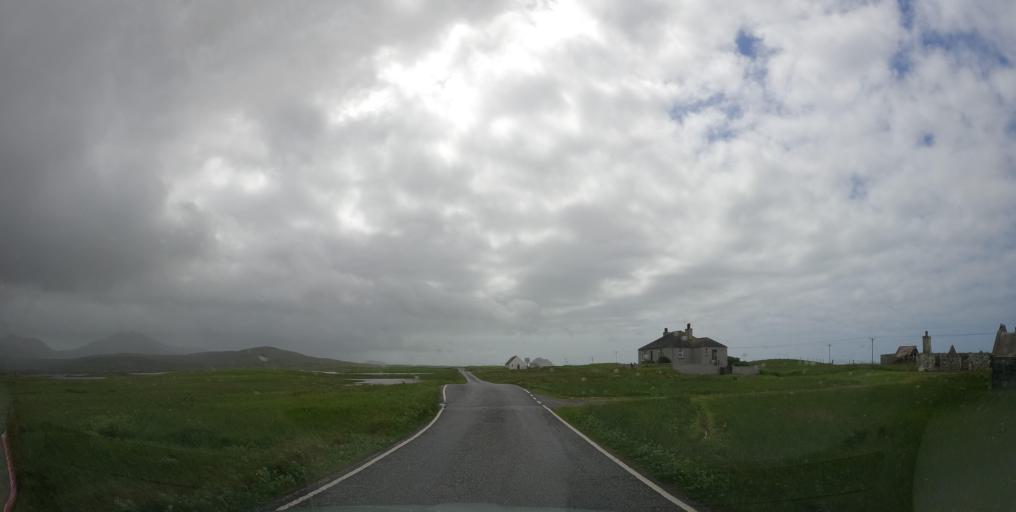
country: GB
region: Scotland
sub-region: Eilean Siar
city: Isle of South Uist
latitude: 57.3231
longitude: -7.3681
